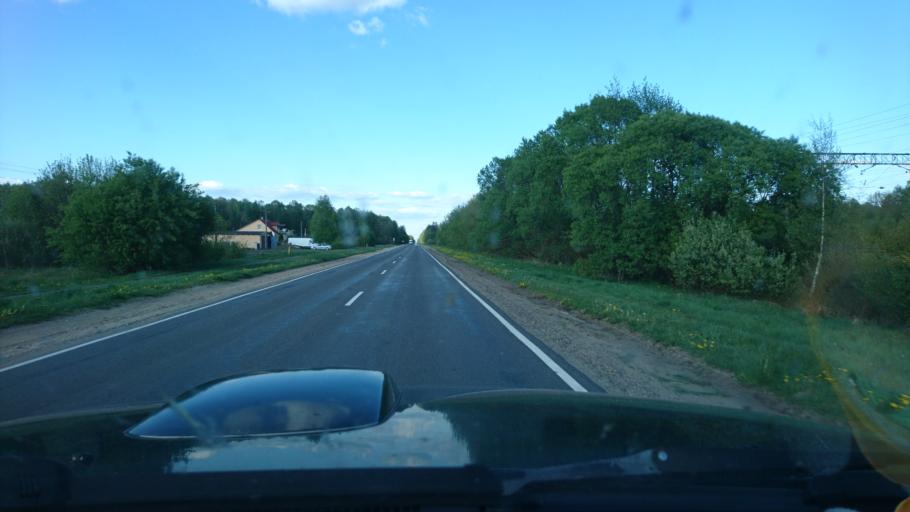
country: BY
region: Brest
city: Nyakhachava
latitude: 52.6527
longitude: 25.2231
